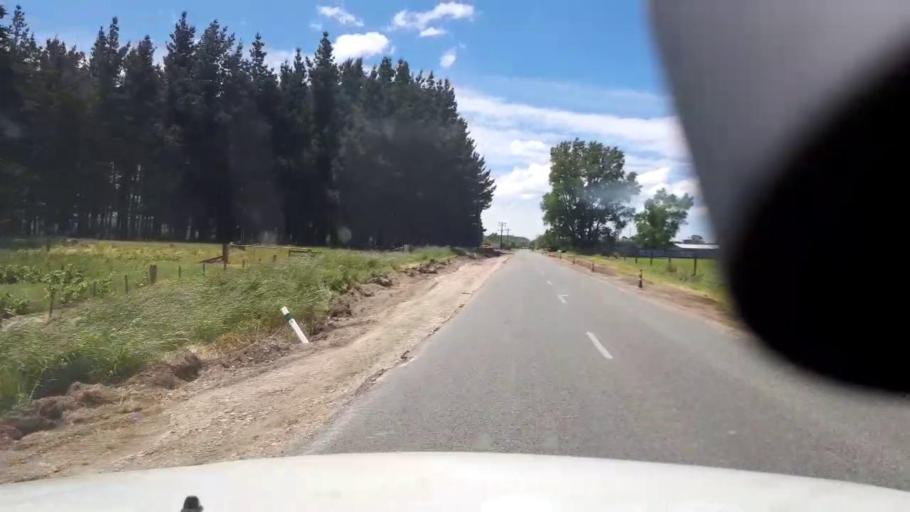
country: NZ
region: Canterbury
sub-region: Timaru District
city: Pleasant Point
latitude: -44.2762
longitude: 171.2511
